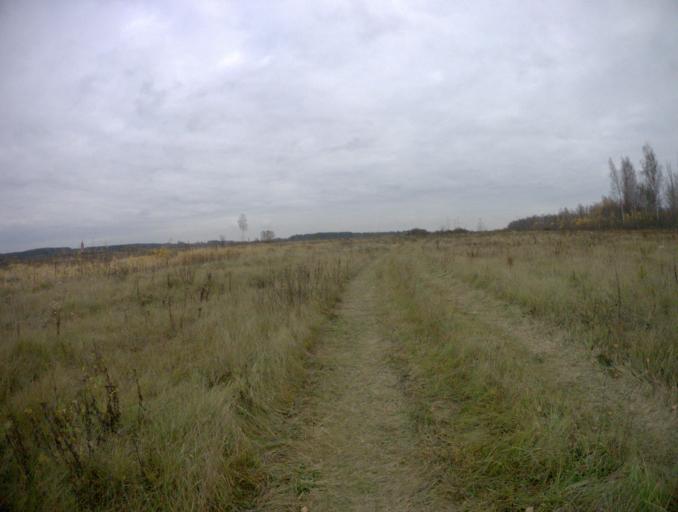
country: RU
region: Moskovskaya
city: Malaya Dubna
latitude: 55.9897
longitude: 38.9784
